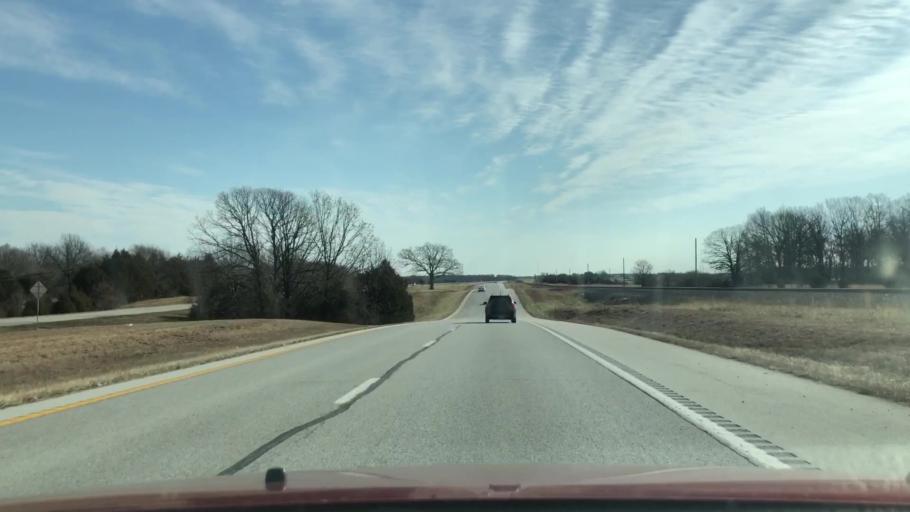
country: US
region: Missouri
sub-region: Webster County
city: Seymour
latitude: 37.1301
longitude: -92.7178
